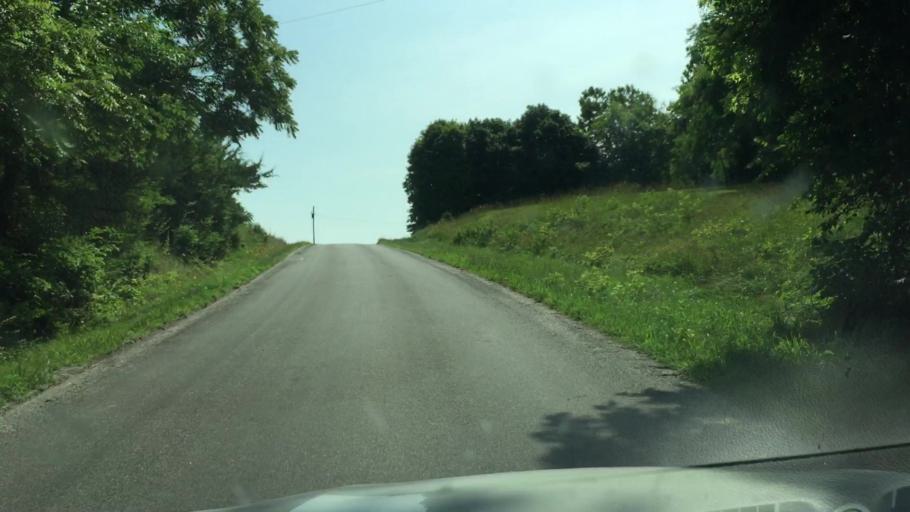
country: US
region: Illinois
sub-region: Hancock County
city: Nauvoo
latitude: 40.5120
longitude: -91.3571
